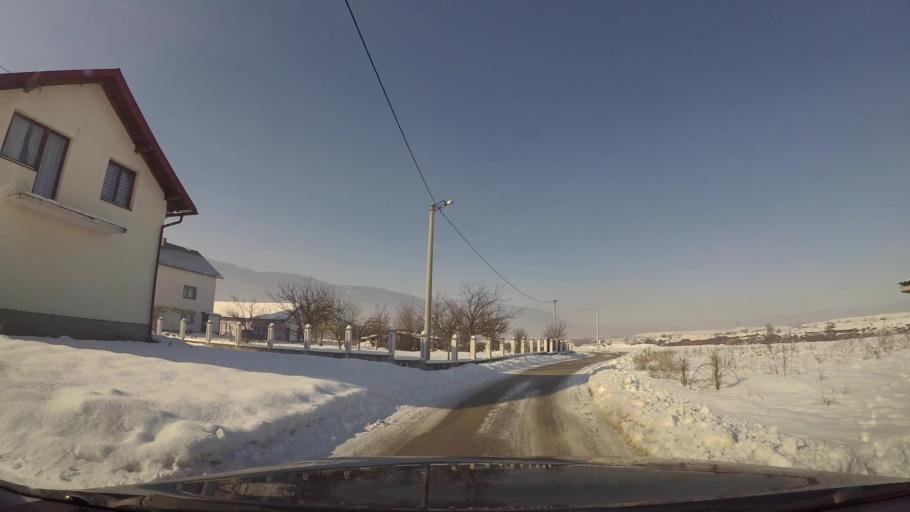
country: BA
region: Federation of Bosnia and Herzegovina
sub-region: Kanton Sarajevo
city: Sarajevo
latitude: 43.7999
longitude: 18.3400
